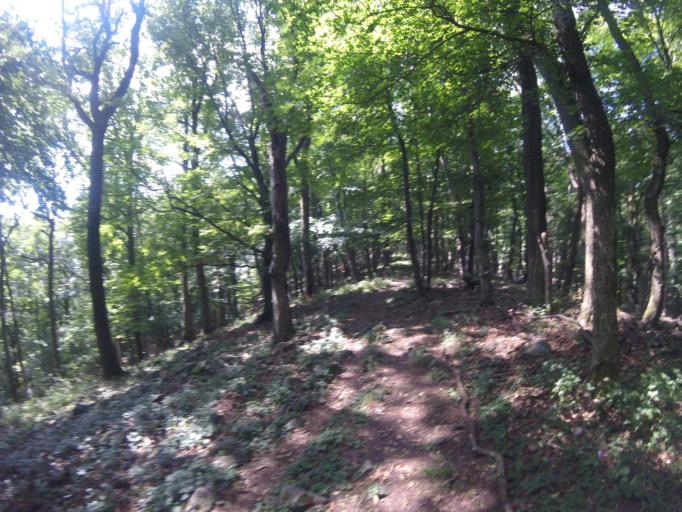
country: SK
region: Nitriansky
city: Sahy
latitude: 47.9745
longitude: 18.8855
